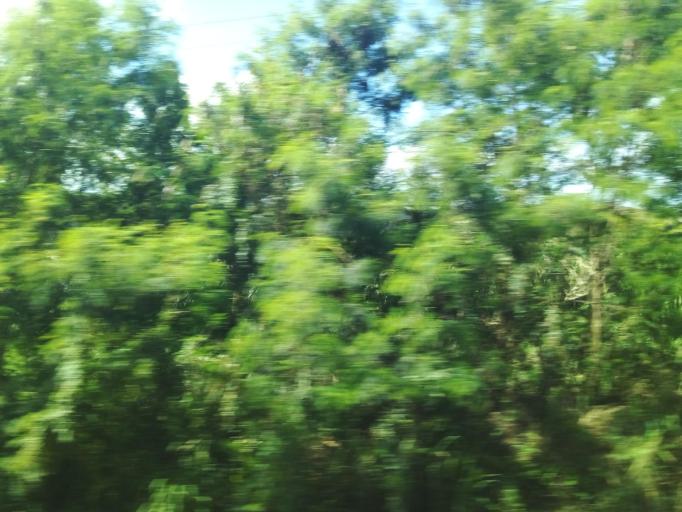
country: BR
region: Minas Gerais
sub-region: Governador Valadares
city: Governador Valadares
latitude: -18.8711
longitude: -41.7646
